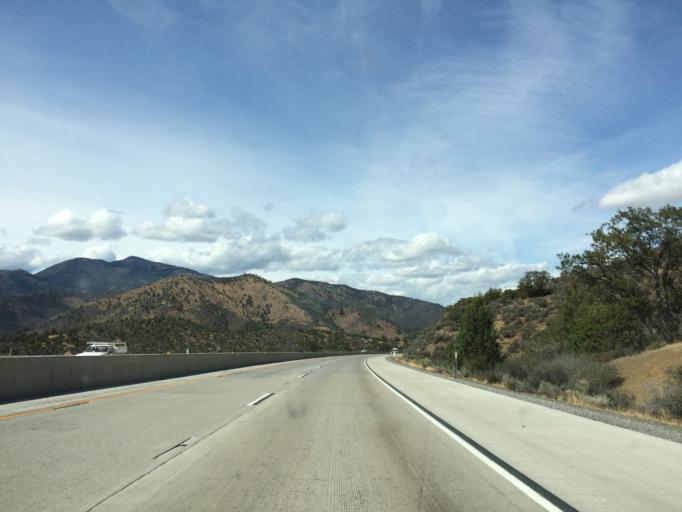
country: US
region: California
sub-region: Siskiyou County
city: Yreka
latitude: 41.8181
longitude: -122.5770
